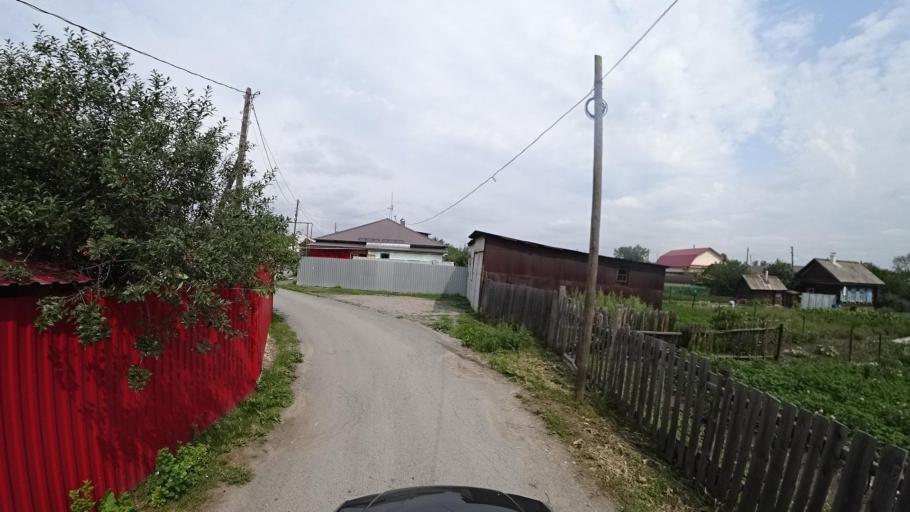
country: RU
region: Sverdlovsk
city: Kamyshlov
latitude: 56.8470
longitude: 62.6779
